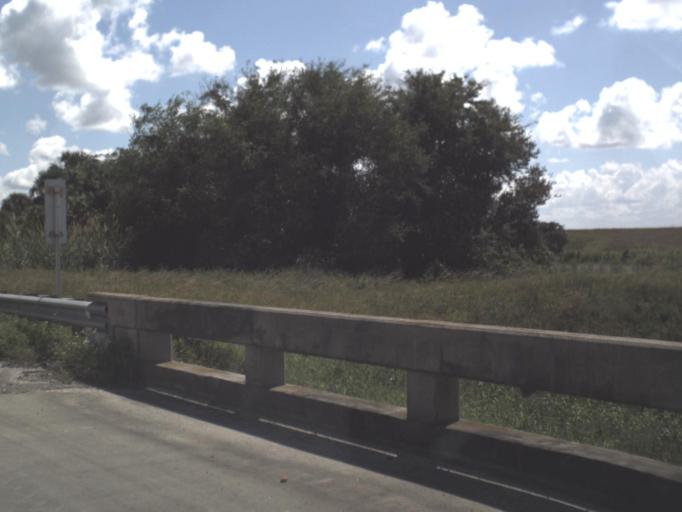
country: US
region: Florida
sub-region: Okeechobee County
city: Taylor Creek
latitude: 27.1935
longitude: -80.7612
